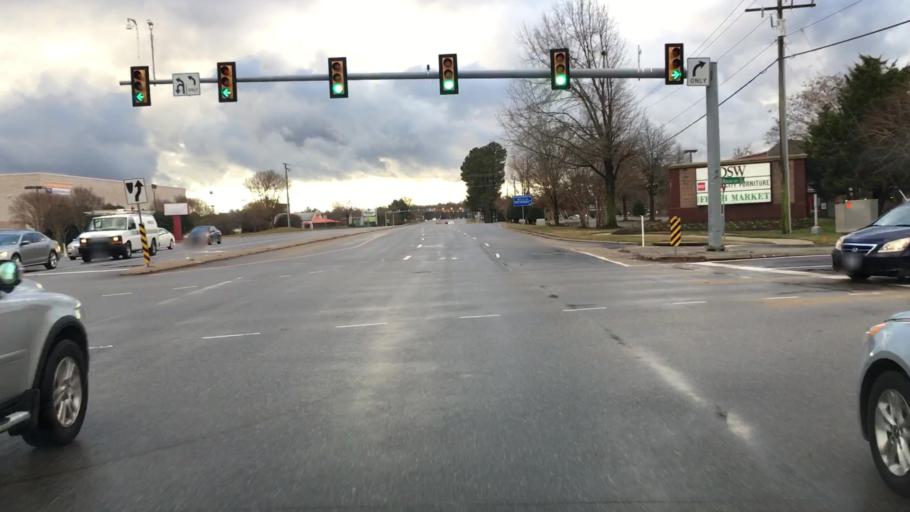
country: US
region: Virginia
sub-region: Chesterfield County
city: Bon Air
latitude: 37.5111
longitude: -77.6143
